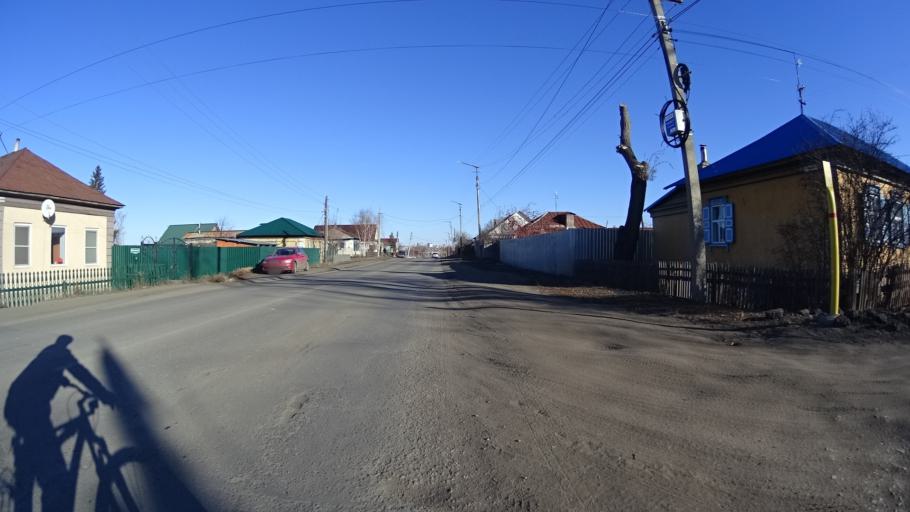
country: RU
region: Chelyabinsk
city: Troitsk
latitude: 54.0858
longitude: 61.5270
